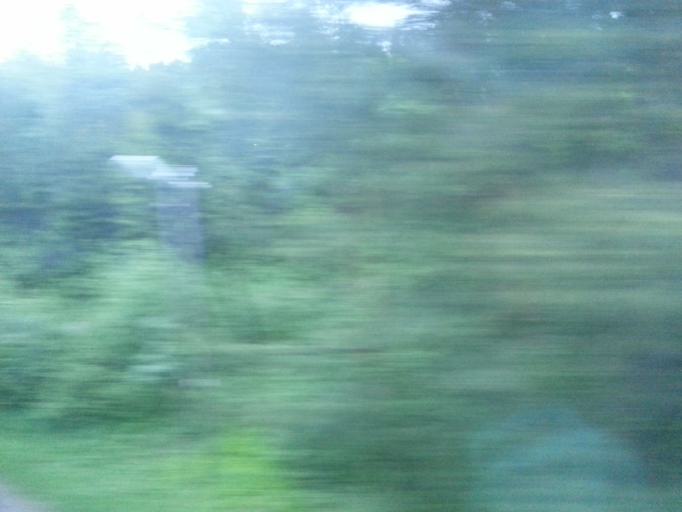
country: NO
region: Oppland
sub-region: Dovre
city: Dombas
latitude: 62.0739
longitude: 9.1301
